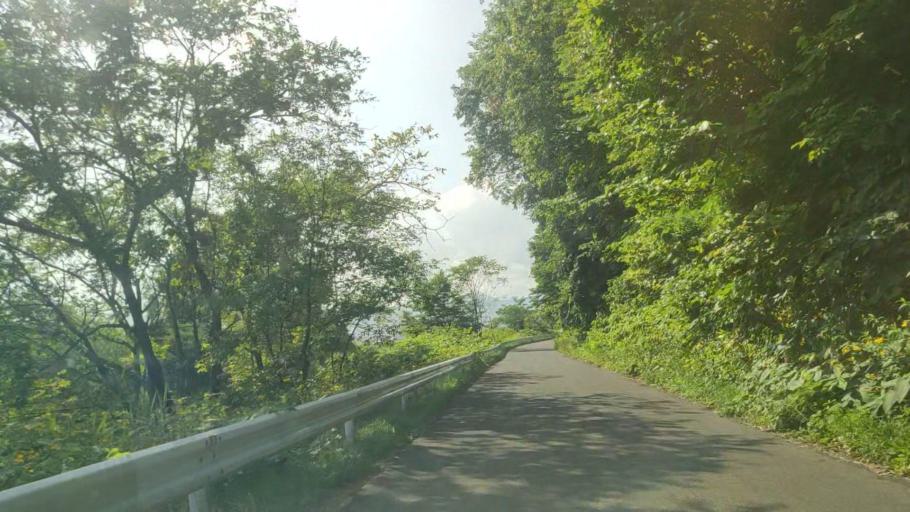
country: JP
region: Hokkaido
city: Shimo-furano
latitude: 43.3411
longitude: 142.3746
